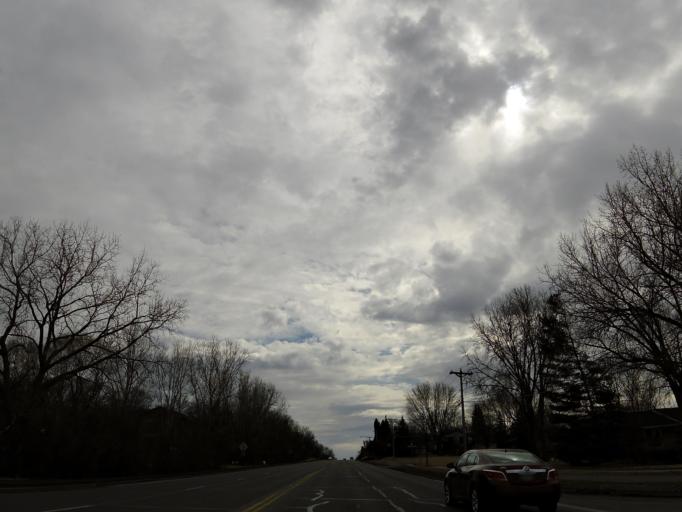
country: US
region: Minnesota
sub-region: Hennepin County
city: Bloomington
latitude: 44.8252
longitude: -93.3295
